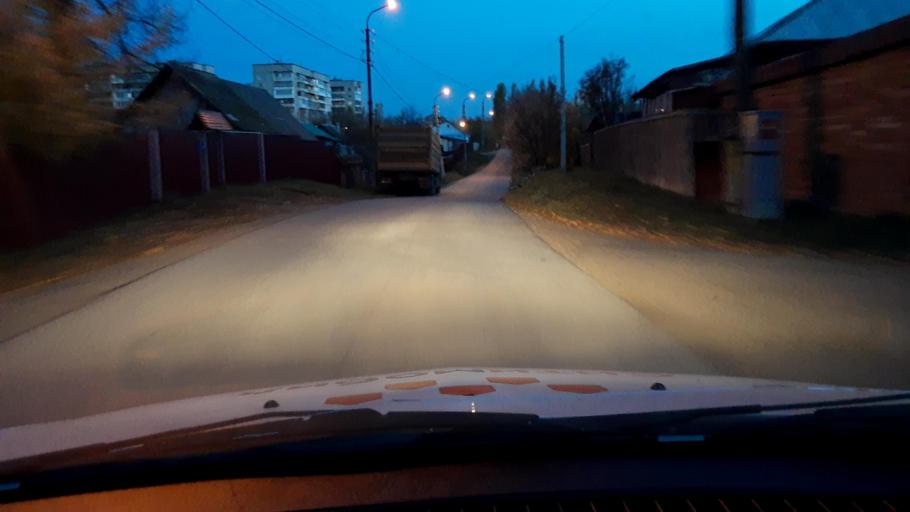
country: RU
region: Bashkortostan
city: Iglino
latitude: 54.7650
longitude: 56.2279
